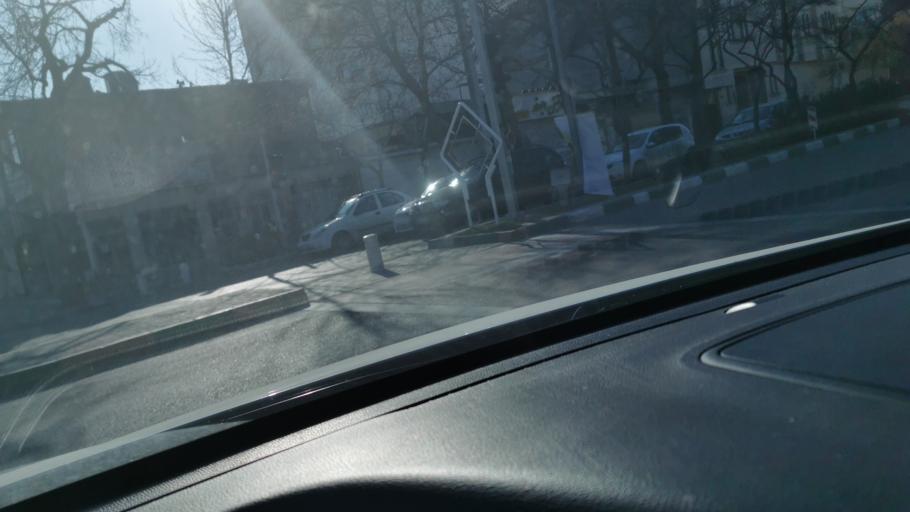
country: IR
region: Razavi Khorasan
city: Mashhad
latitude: 36.2925
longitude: 59.5649
